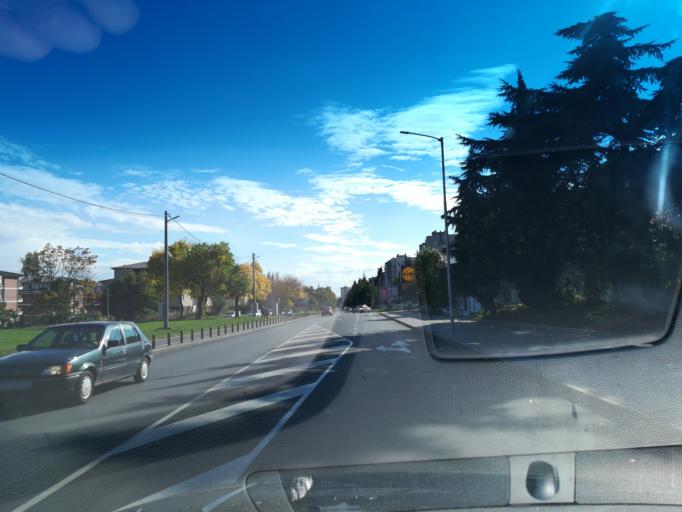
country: BG
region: Stara Zagora
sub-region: Obshtina Stara Zagora
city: Stara Zagora
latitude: 42.4397
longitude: 25.6354
